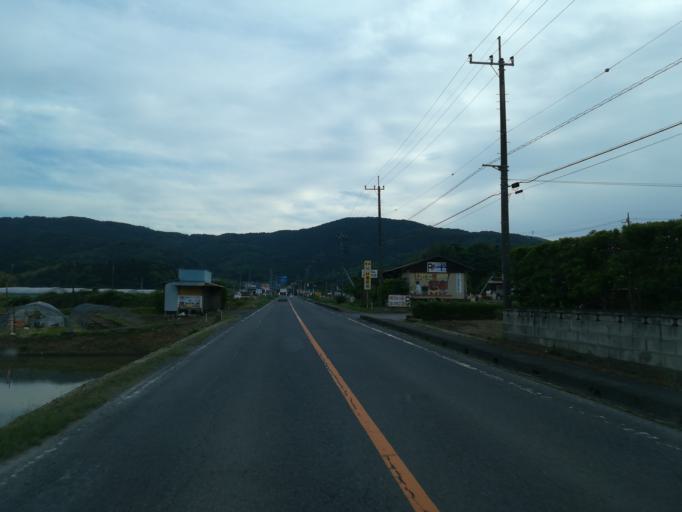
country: JP
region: Ibaraki
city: Tsukuba
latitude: 36.1900
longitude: 140.1723
